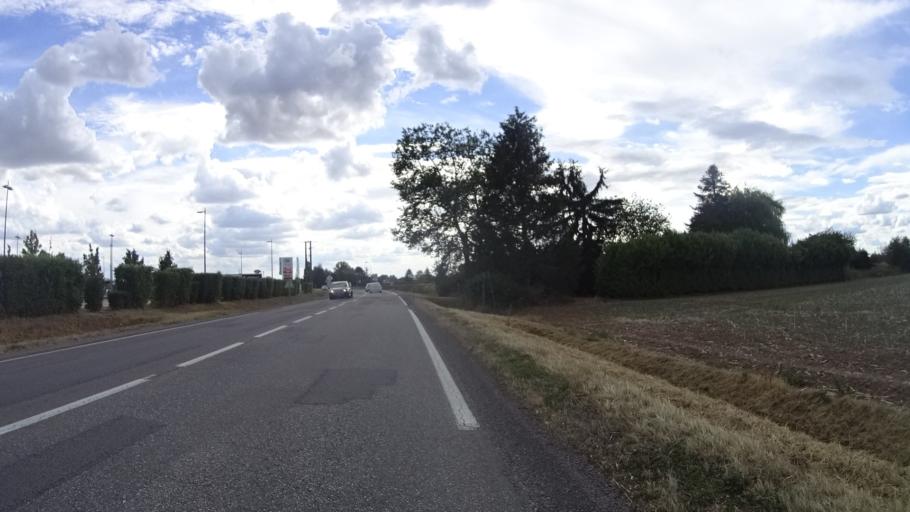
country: FR
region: Bourgogne
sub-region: Departement de la Cote-d'Or
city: Seurre
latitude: 47.0106
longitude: 5.1569
